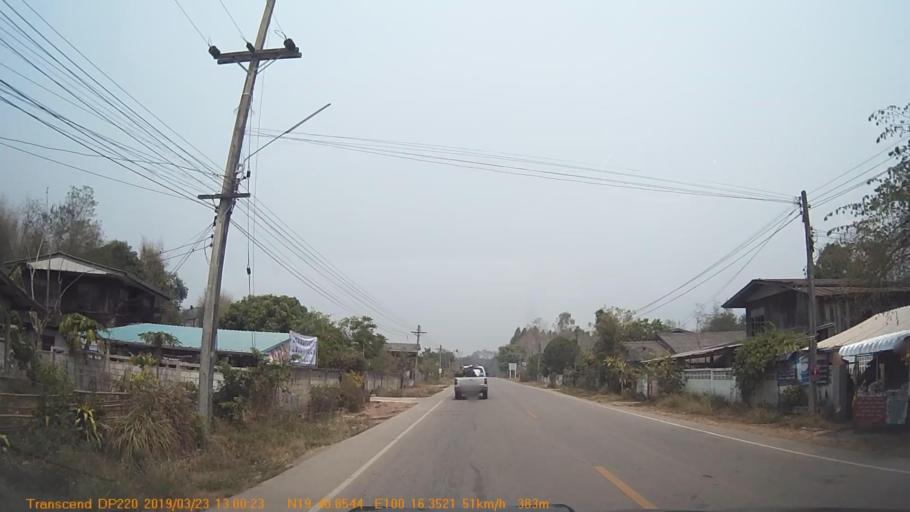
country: TH
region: Chiang Rai
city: Thoeng
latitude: 19.6811
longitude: 100.2728
